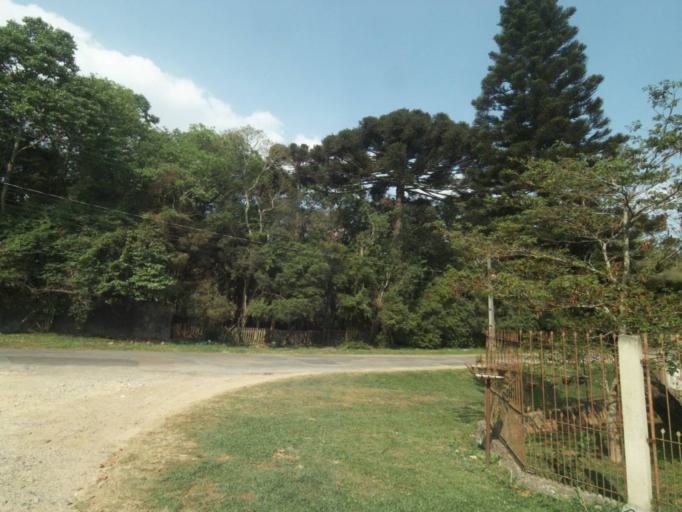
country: BR
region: Parana
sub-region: Sao Jose Dos Pinhais
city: Sao Jose dos Pinhais
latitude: -25.5170
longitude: -49.2465
